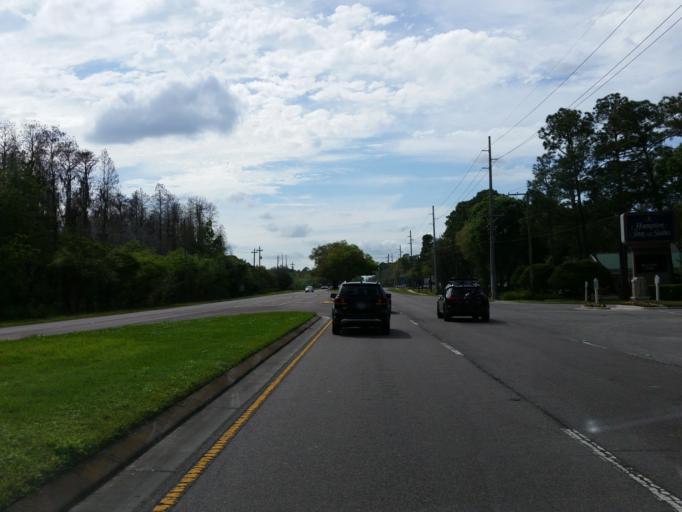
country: US
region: Florida
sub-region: Hillsborough County
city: Temple Terrace
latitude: 28.0693
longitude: -82.3643
